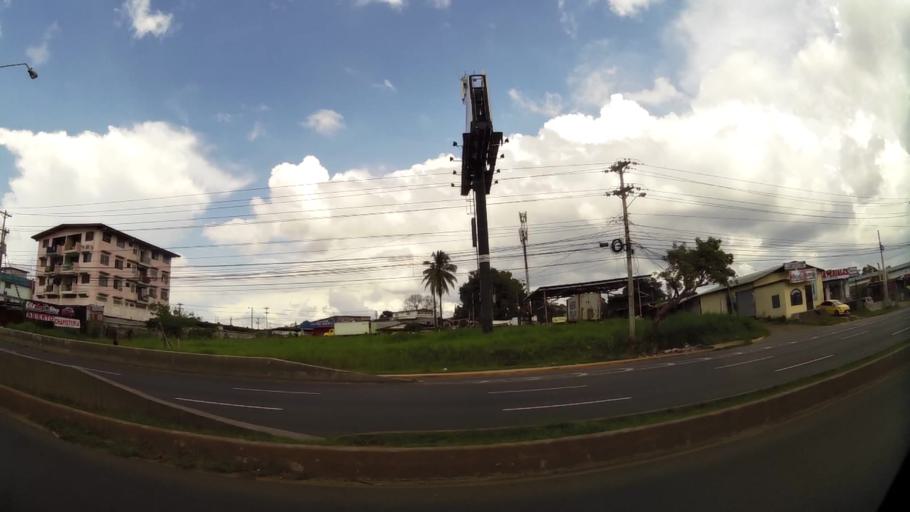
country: PA
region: Panama
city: San Miguelito
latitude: 9.0591
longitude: -79.4310
